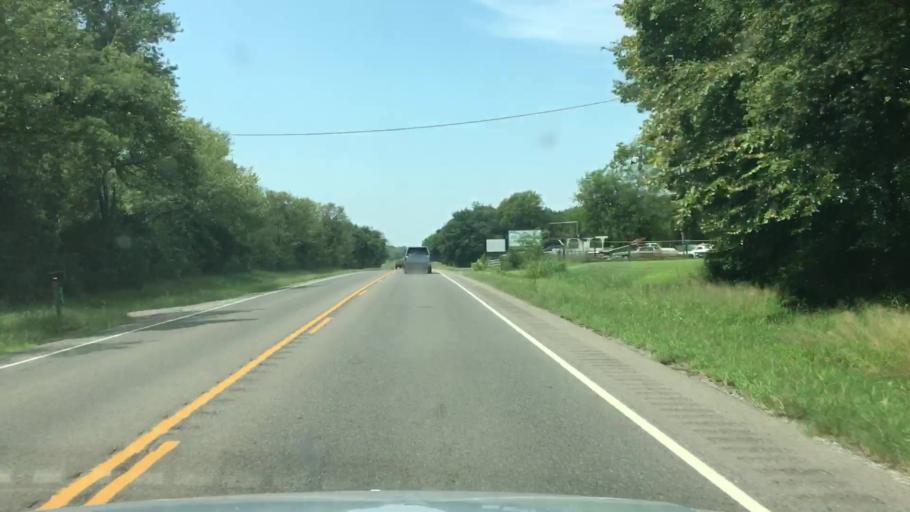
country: US
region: Oklahoma
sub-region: Wagoner County
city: Wagoner
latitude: 35.9371
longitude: -95.3191
